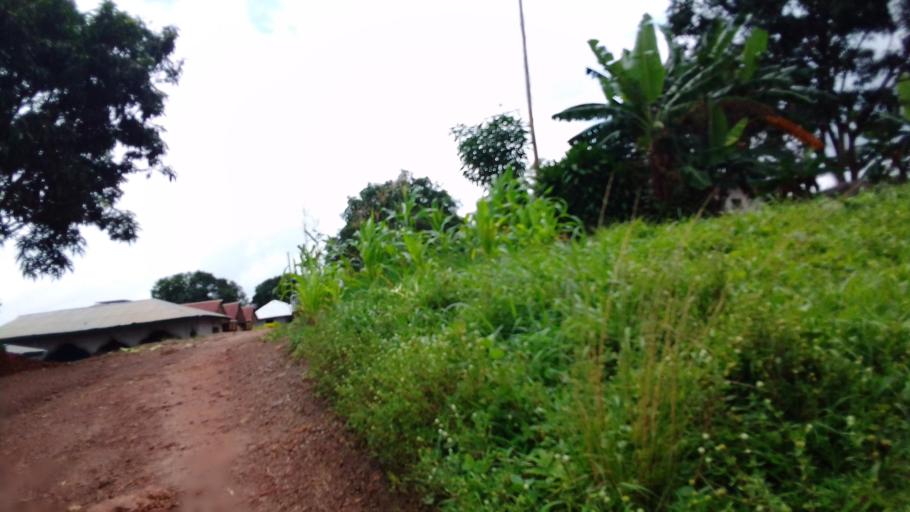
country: SL
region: Eastern Province
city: Kenema
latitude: 7.8618
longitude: -11.1752
